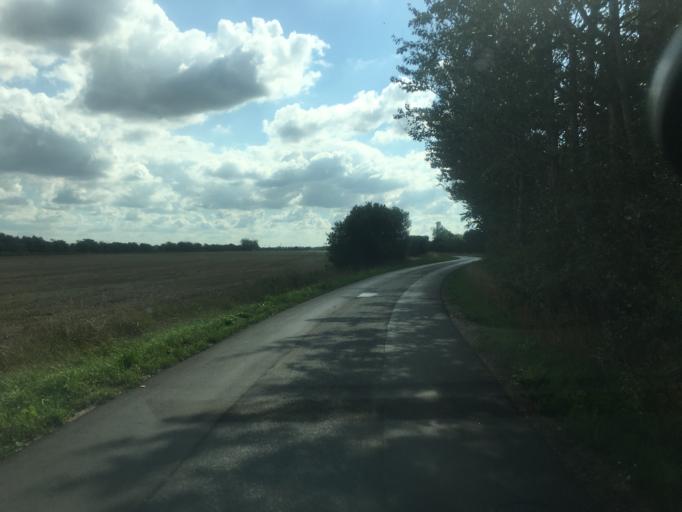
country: DK
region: South Denmark
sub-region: Tonder Kommune
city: Logumkloster
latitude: 54.9862
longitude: 8.9987
